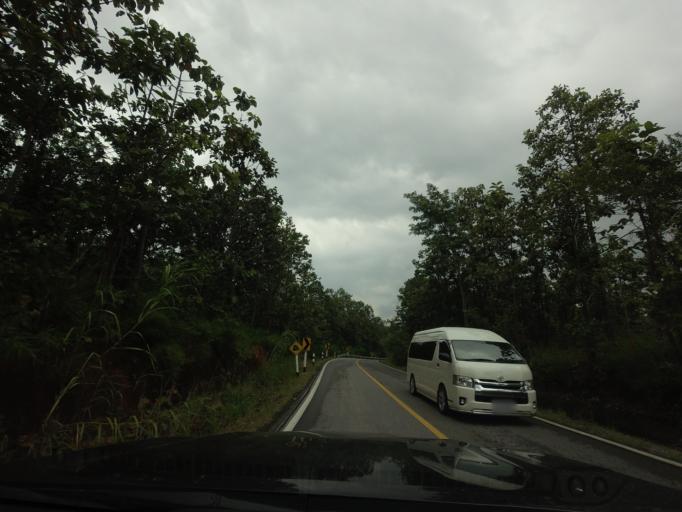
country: TH
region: Nong Khai
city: Sangkhom
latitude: 18.0305
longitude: 102.3413
